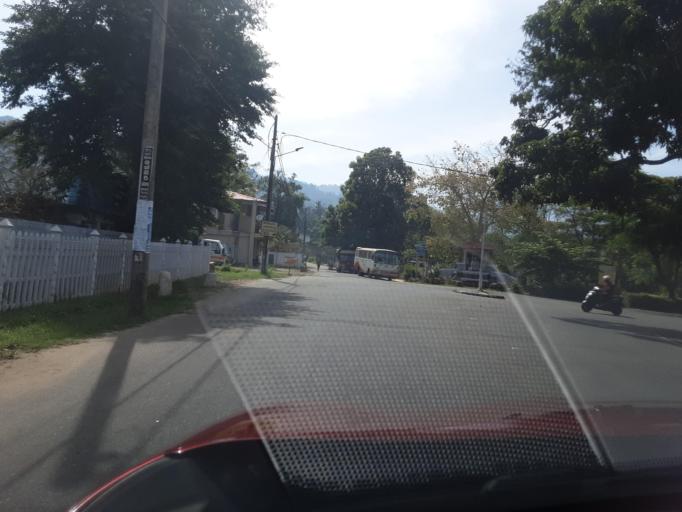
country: LK
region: Uva
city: Badulla
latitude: 6.9879
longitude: 81.0635
